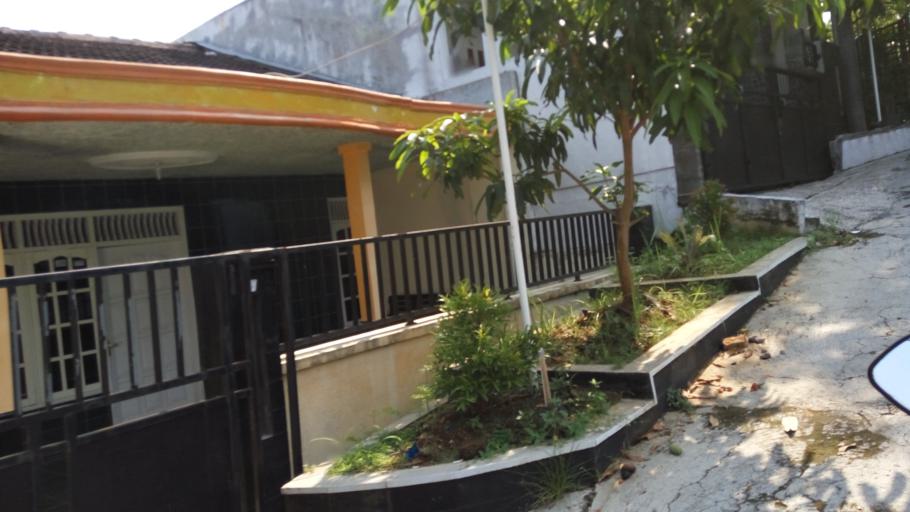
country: ID
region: Central Java
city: Mranggen
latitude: -7.0315
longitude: 110.4737
